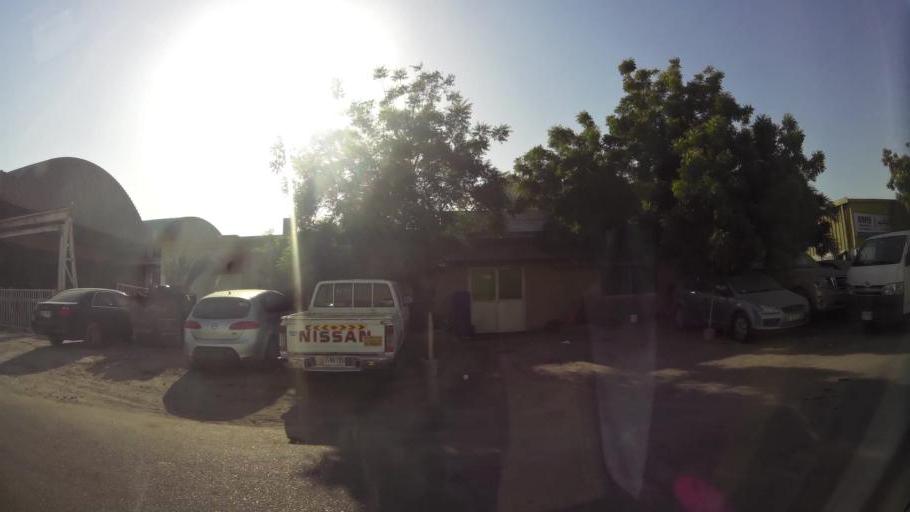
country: AE
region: Ash Shariqah
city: Sharjah
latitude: 25.2887
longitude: 55.3887
